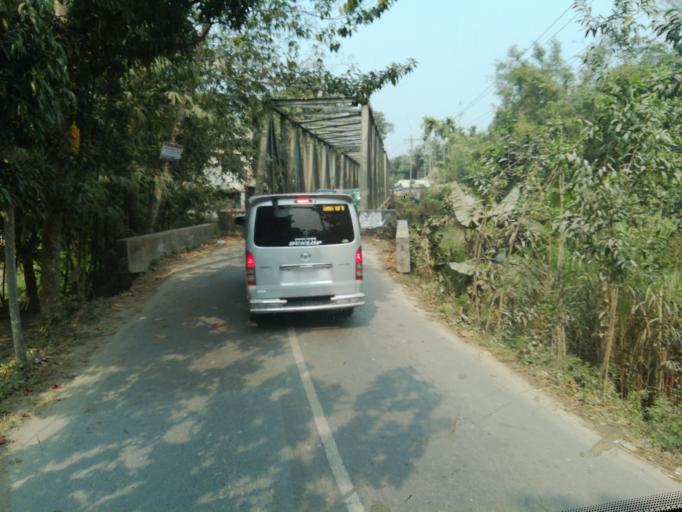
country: BD
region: Dhaka
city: Nagarpur
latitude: 24.0002
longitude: 89.8470
